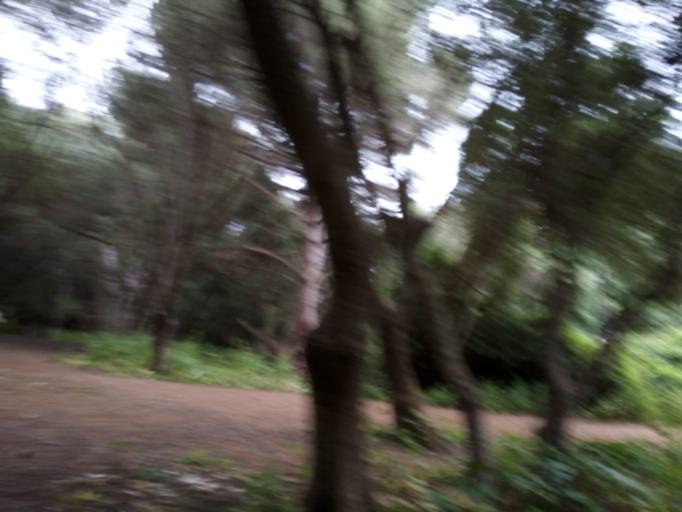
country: DZ
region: Tipaza
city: Tipasa
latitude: 36.5933
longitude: 2.4418
